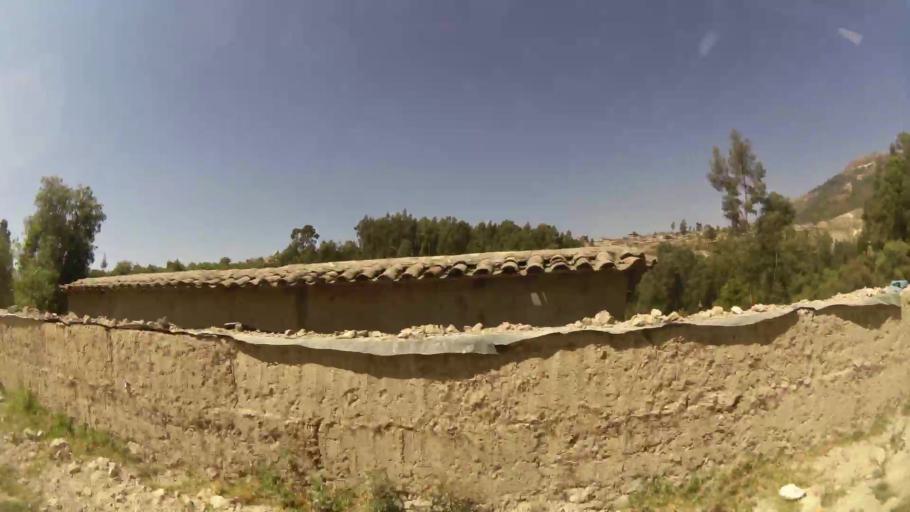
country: PE
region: Ayacucho
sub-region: Provincia de Huamanga
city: Carmen Alto
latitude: -13.1792
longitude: -74.2309
